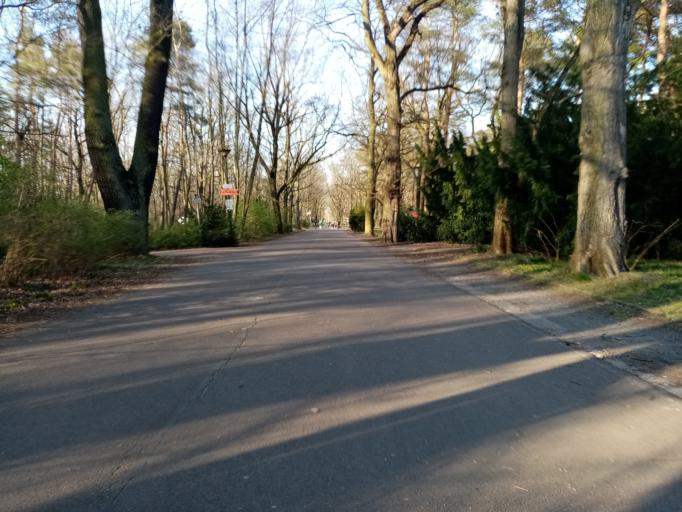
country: DE
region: Berlin
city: Karlshorst
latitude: 52.4643
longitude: 13.5472
